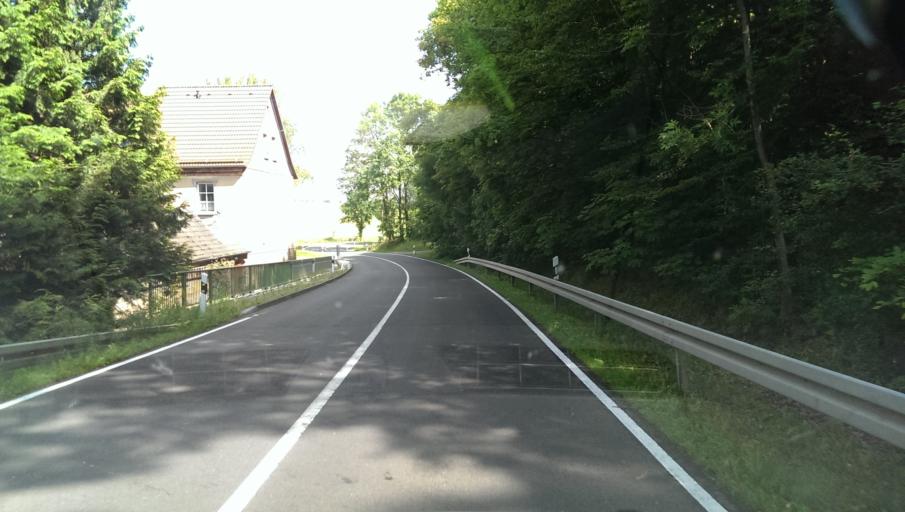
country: DE
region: Saxony-Anhalt
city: Eckartsberga
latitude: 51.1510
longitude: 11.5626
